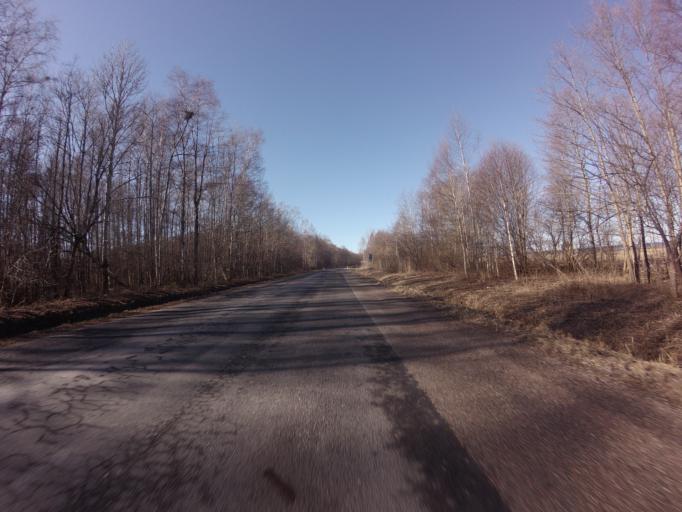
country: EE
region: Saare
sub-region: Kuressaare linn
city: Kuressaare
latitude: 58.5812
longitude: 22.6247
